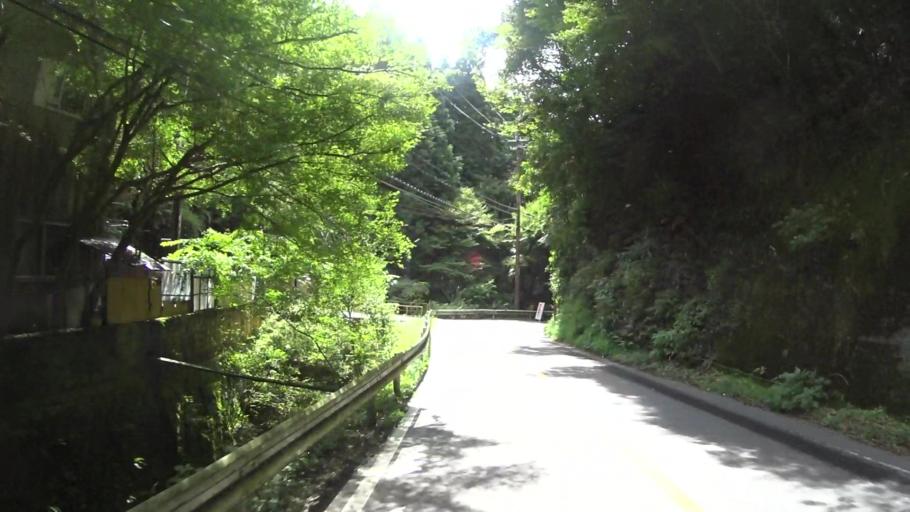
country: JP
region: Kyoto
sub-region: Kyoto-shi
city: Kamigyo-ku
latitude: 35.0321
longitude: 135.8074
